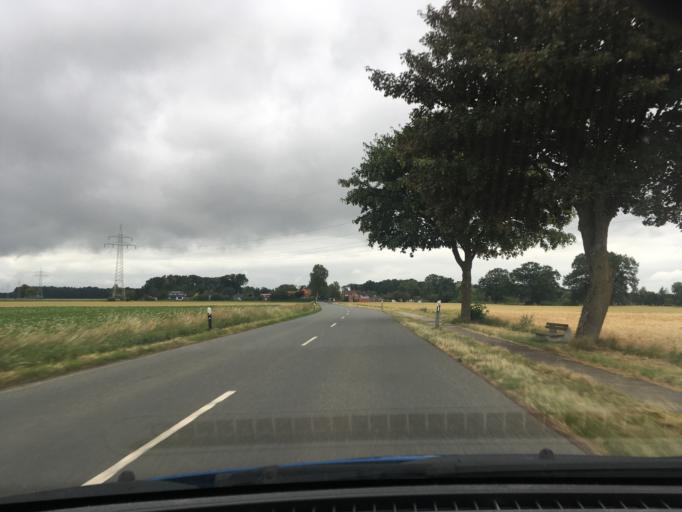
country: DE
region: Lower Saxony
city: Soderstorf
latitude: 53.1685
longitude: 10.1587
